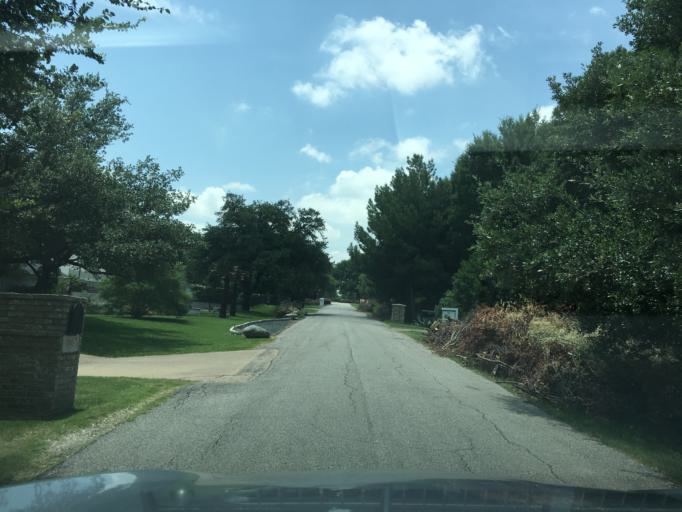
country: US
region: Texas
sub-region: Dallas County
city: Addison
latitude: 32.9153
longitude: -96.7899
